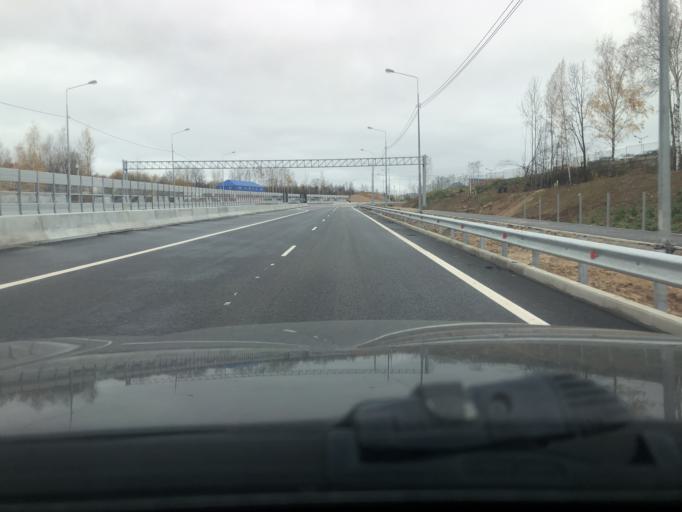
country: RU
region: Moskovskaya
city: Sergiyev Posad
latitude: 56.3391
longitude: 38.1219
